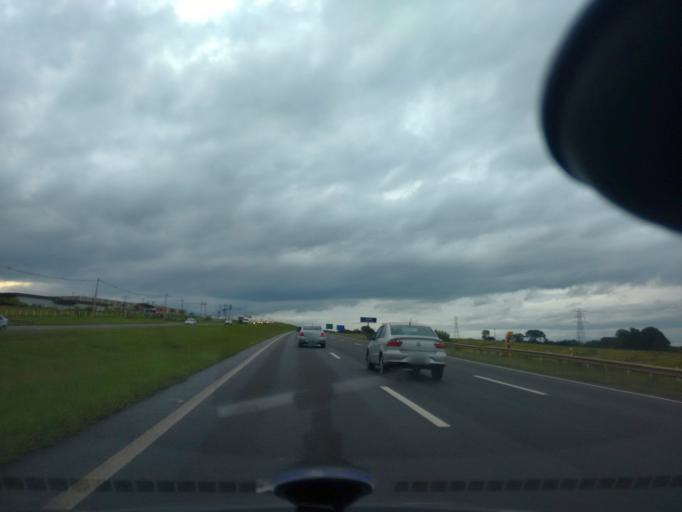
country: BR
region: Sao Paulo
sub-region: Santa Gertrudes
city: Santa Gertrudes
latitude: -22.4480
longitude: -47.5603
